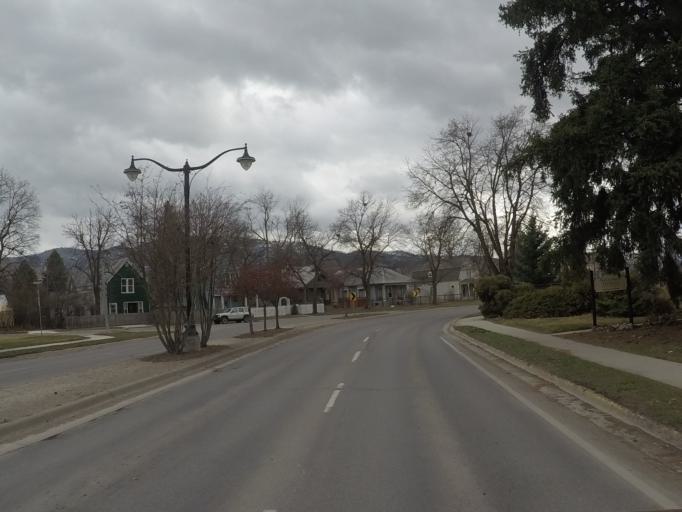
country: US
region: Montana
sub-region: Missoula County
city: Missoula
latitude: 46.8636
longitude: -114.0036
